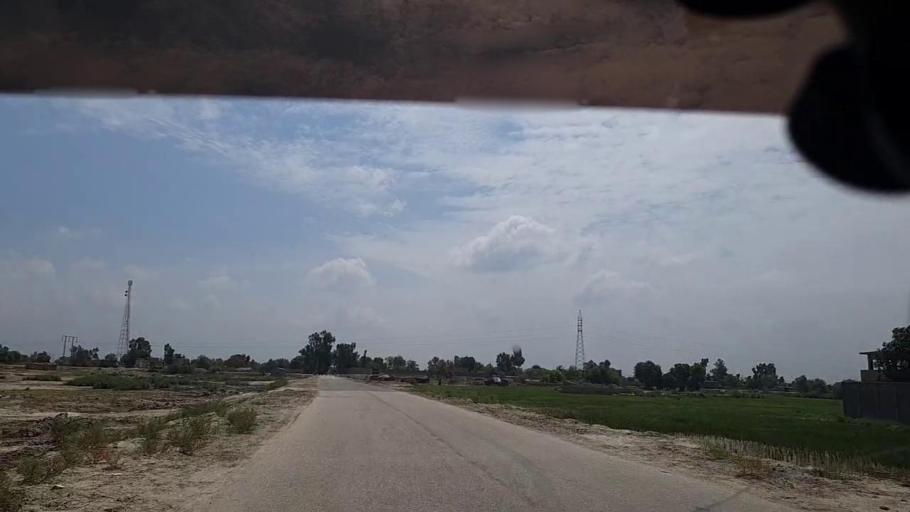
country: PK
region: Sindh
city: Ghauspur
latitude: 28.0905
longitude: 68.9611
